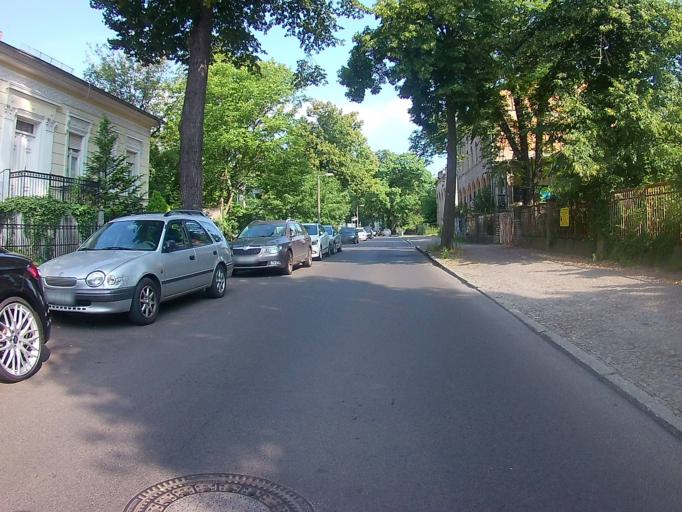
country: DE
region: Berlin
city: Grunau
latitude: 52.4141
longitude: 13.5831
